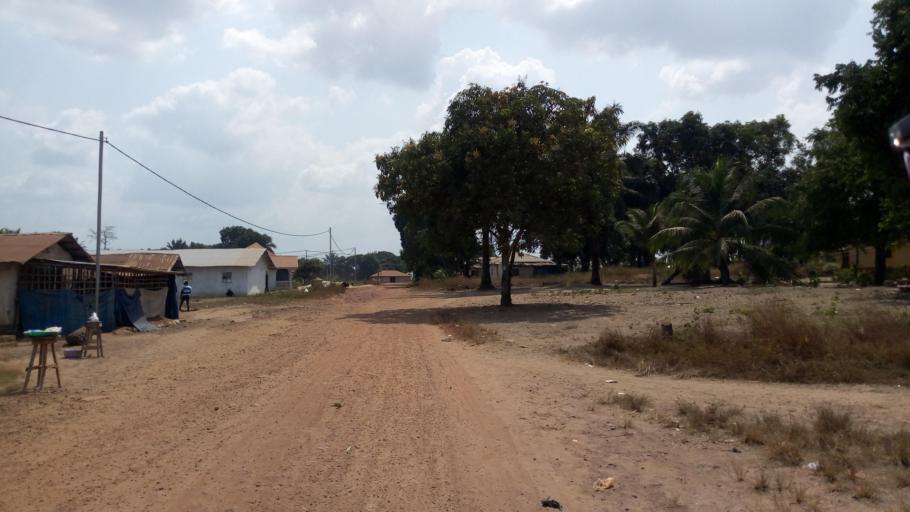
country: SL
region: Southern Province
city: Mogbwemo
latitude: 7.7913
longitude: -12.3018
